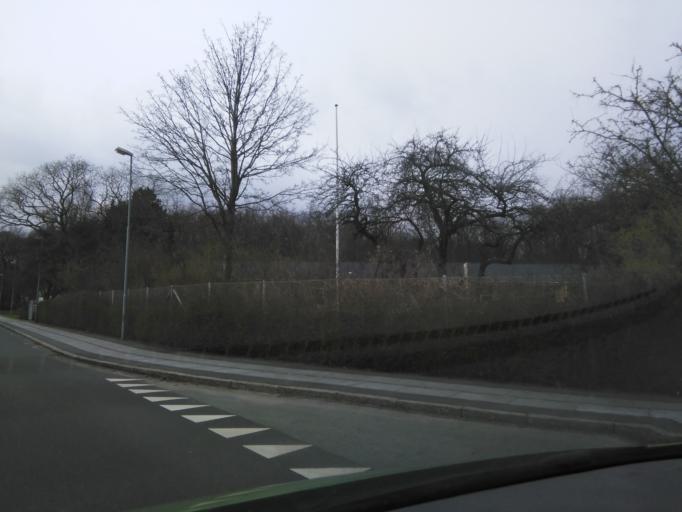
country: DK
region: Central Jutland
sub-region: Arhus Kommune
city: Arhus
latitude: 56.1190
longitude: 10.2014
